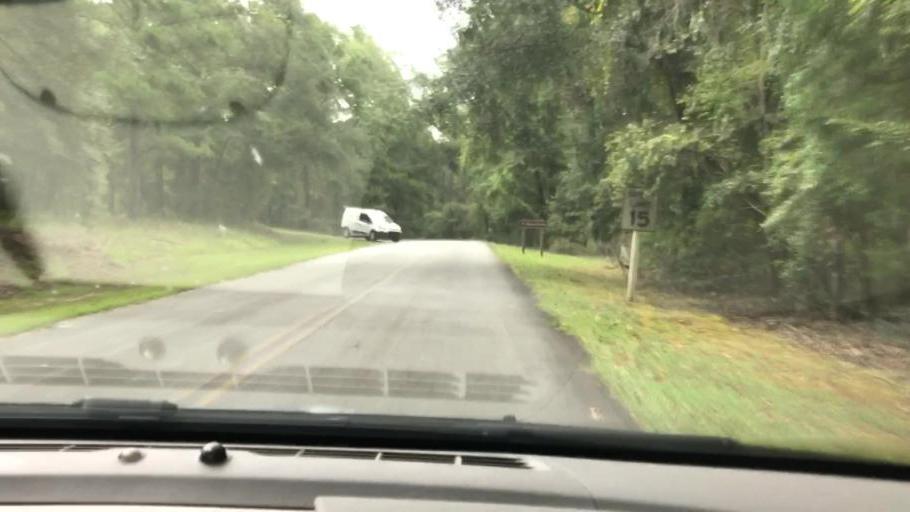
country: US
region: Georgia
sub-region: Clay County
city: Fort Gaines
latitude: 31.6667
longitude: -85.0544
